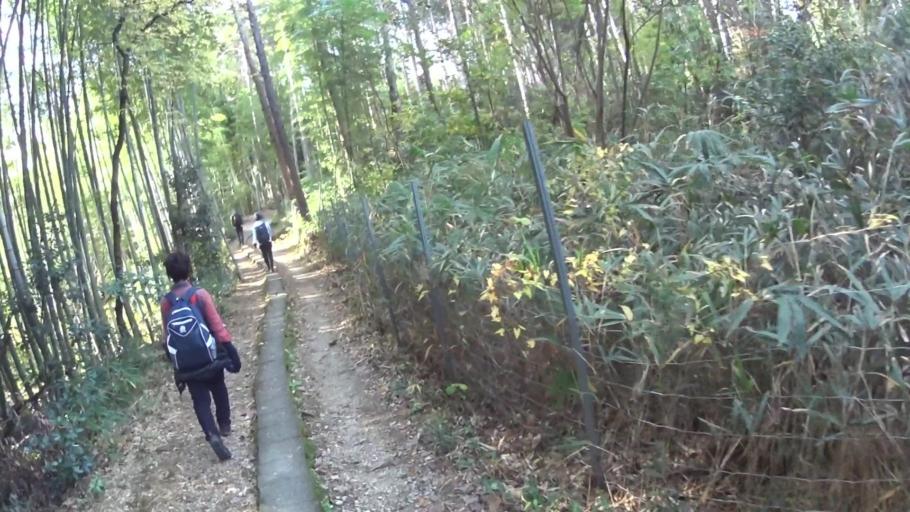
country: JP
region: Kyoto
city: Kyoto
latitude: 34.9662
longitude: 135.7797
